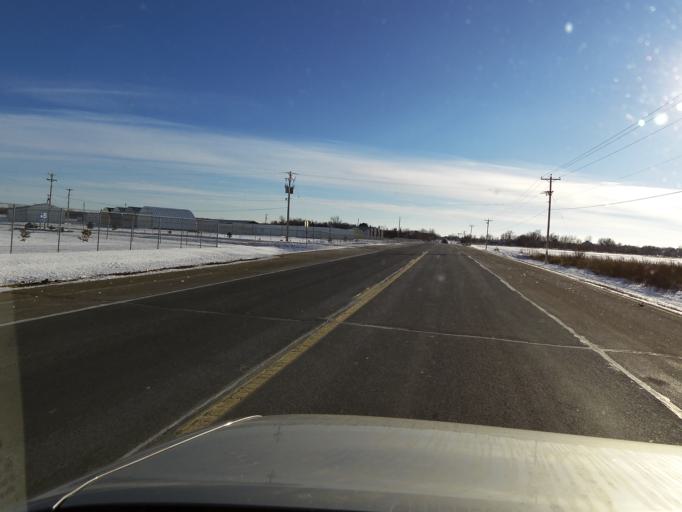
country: US
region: Minnesota
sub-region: Washington County
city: Lake Elmo
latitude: 44.9971
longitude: -92.8628
